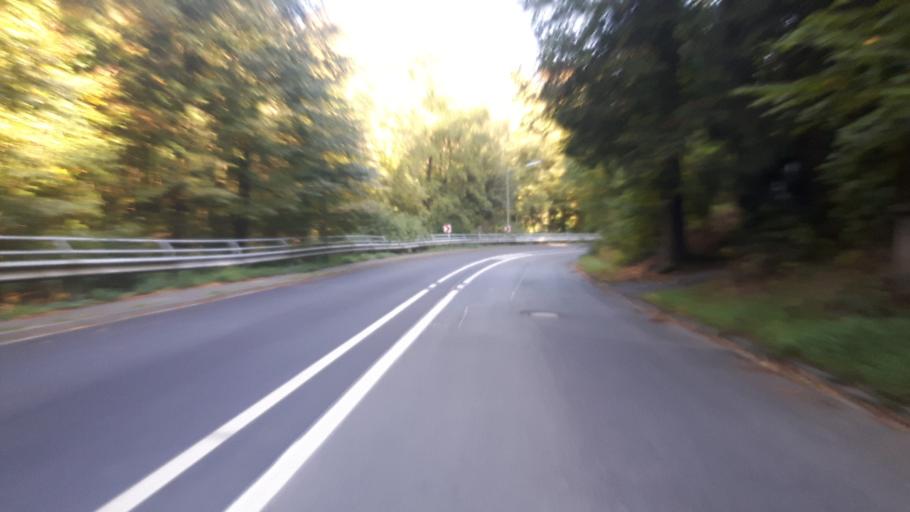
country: DE
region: North Rhine-Westphalia
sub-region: Regierungsbezirk Arnsberg
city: Siegen
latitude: 50.9120
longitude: 8.0374
